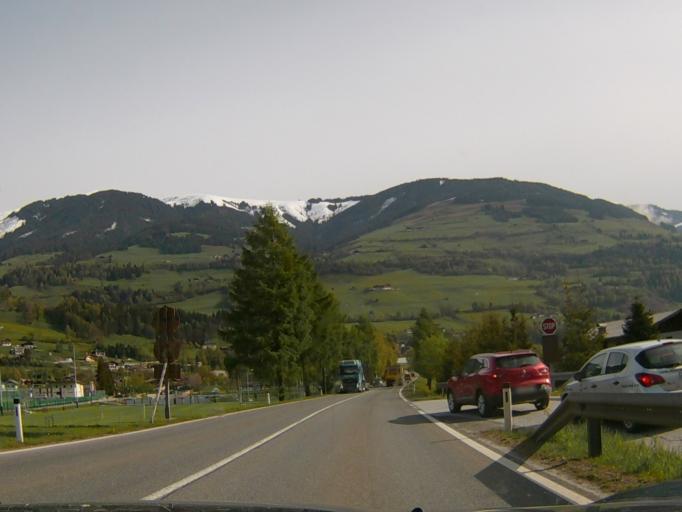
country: AT
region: Salzburg
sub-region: Politischer Bezirk Zell am See
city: Mittersill
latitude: 47.2737
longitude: 12.4880
